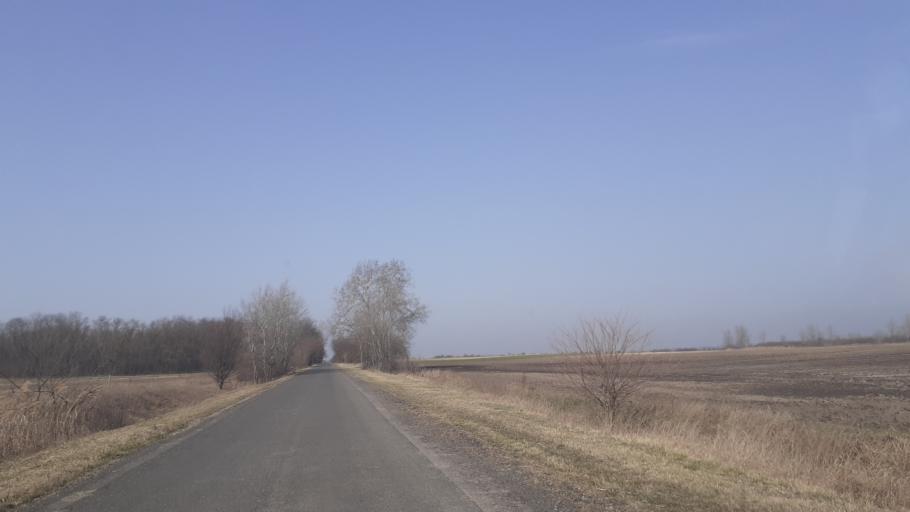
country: HU
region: Pest
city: Dabas
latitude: 47.1198
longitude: 19.2142
